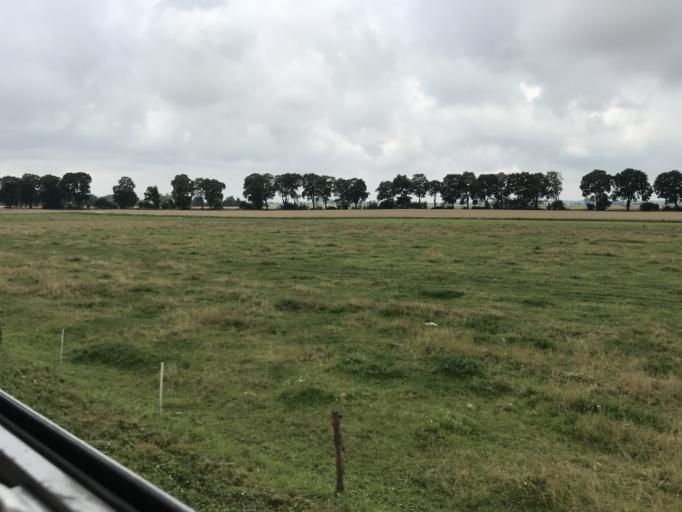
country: PL
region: Pomeranian Voivodeship
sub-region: Powiat malborski
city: Stare Pole
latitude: 54.0589
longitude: 19.2266
